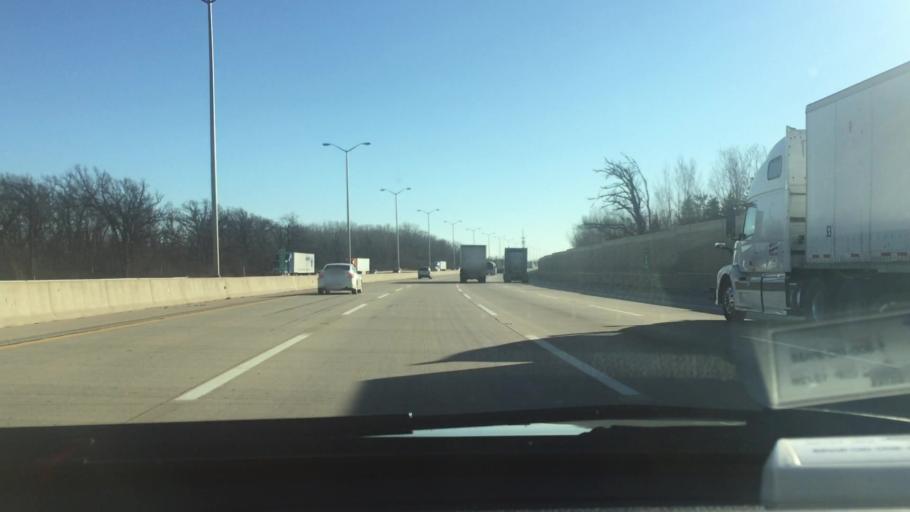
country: US
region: Illinois
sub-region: Lake County
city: Park City
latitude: 42.3270
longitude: -87.9077
